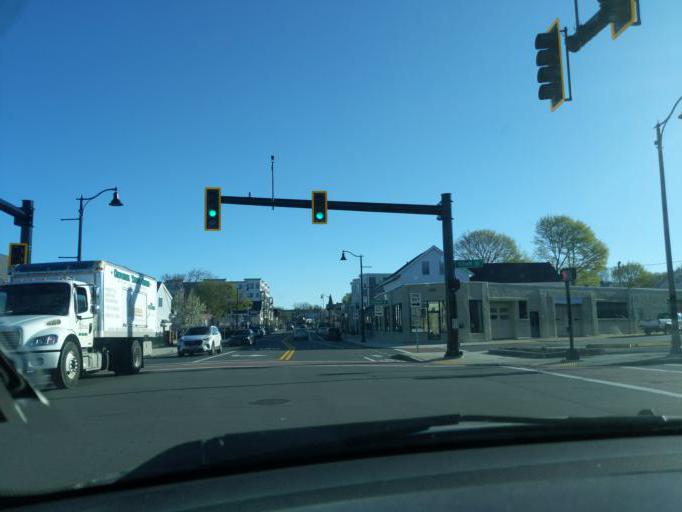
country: US
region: Massachusetts
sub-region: Essex County
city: Beverly
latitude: 42.5544
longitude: -70.8817
